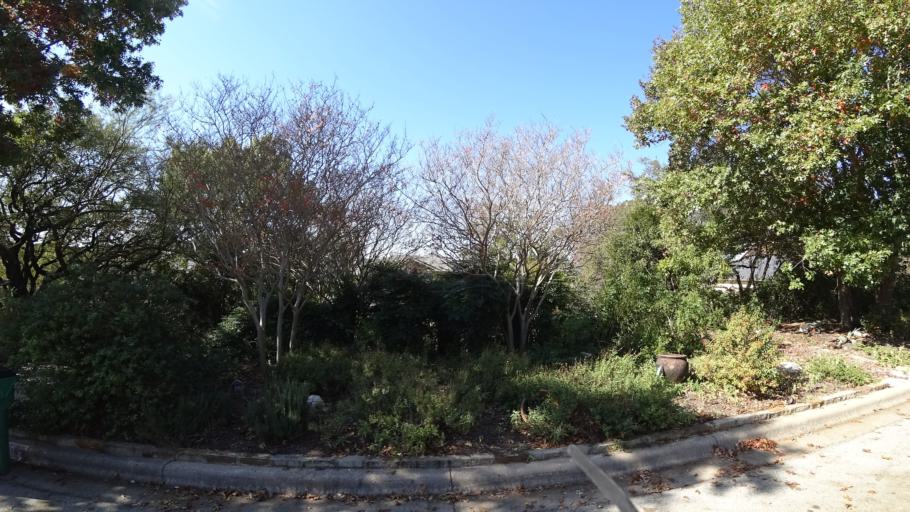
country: US
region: Texas
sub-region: Travis County
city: Lost Creek
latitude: 30.3687
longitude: -97.8633
